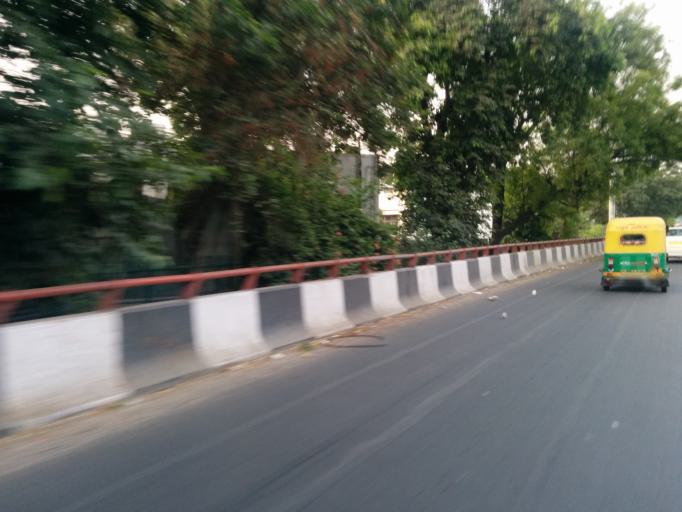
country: IN
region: NCT
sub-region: New Delhi
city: New Delhi
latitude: 28.5700
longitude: 77.2070
